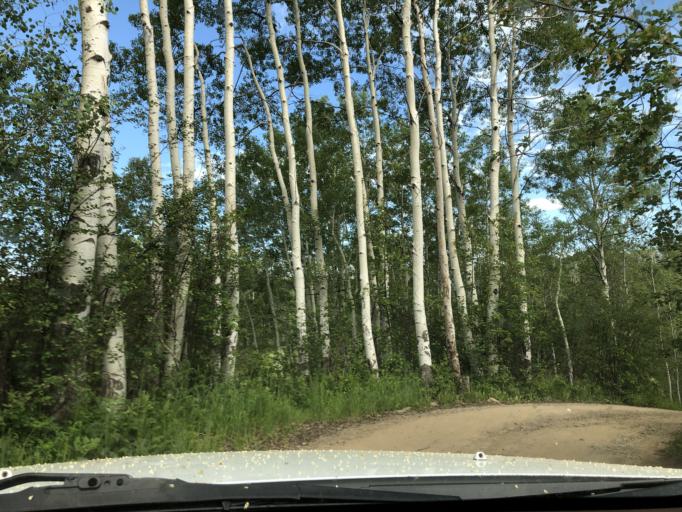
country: US
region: Colorado
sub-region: Delta County
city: Paonia
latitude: 39.0332
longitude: -107.3347
